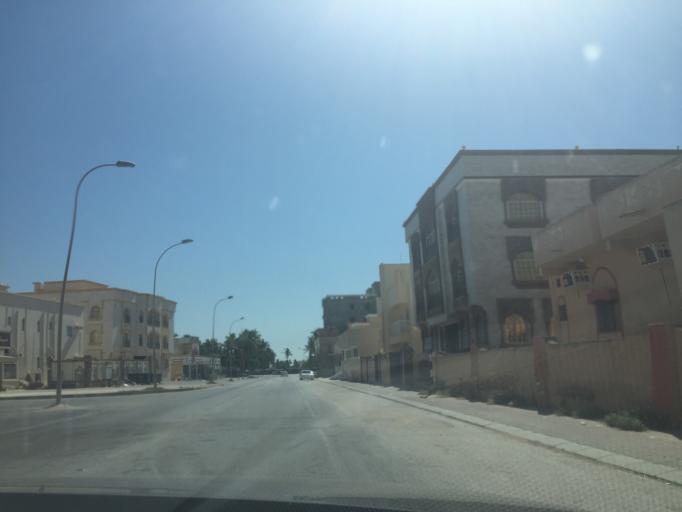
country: OM
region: Zufar
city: Salalah
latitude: 17.0204
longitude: 54.1570
